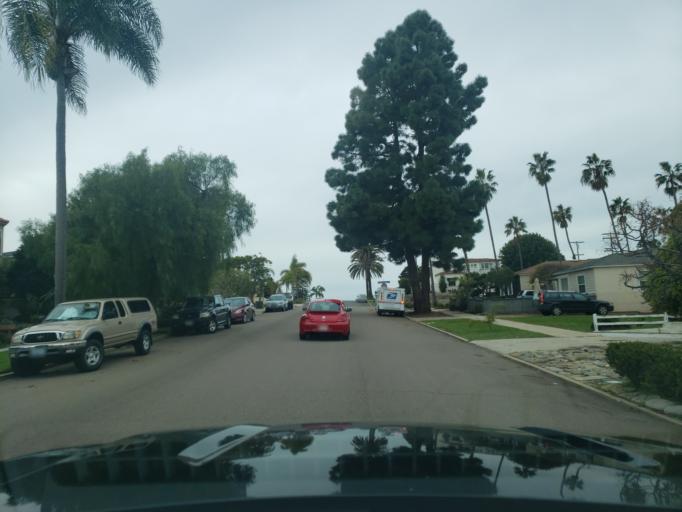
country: US
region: California
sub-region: San Diego County
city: Coronado
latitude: 32.7350
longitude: -117.2444
